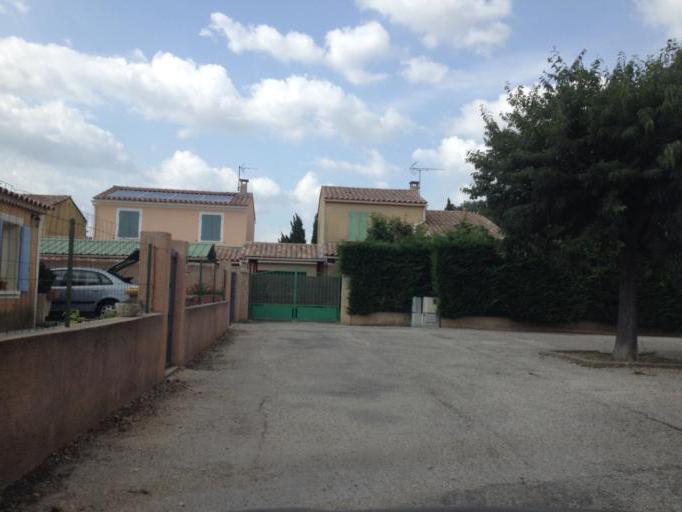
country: FR
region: Provence-Alpes-Cote d'Azur
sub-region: Departement du Vaucluse
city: Orange
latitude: 44.1431
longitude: 4.8186
